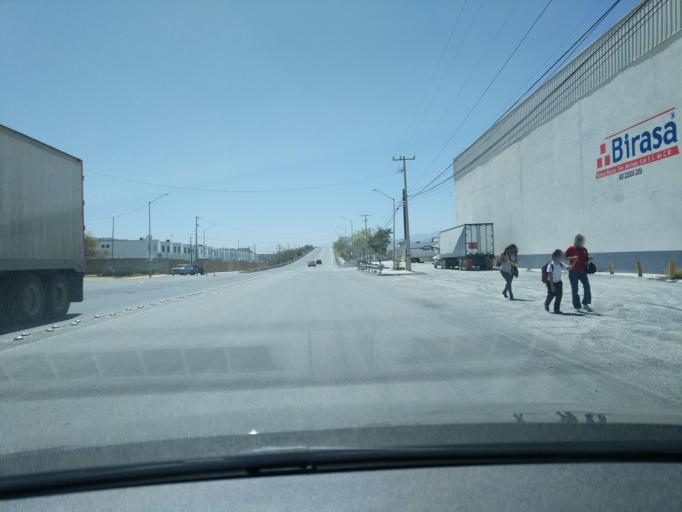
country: MX
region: Nuevo Leon
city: Apodaca
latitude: 25.7982
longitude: -100.1569
